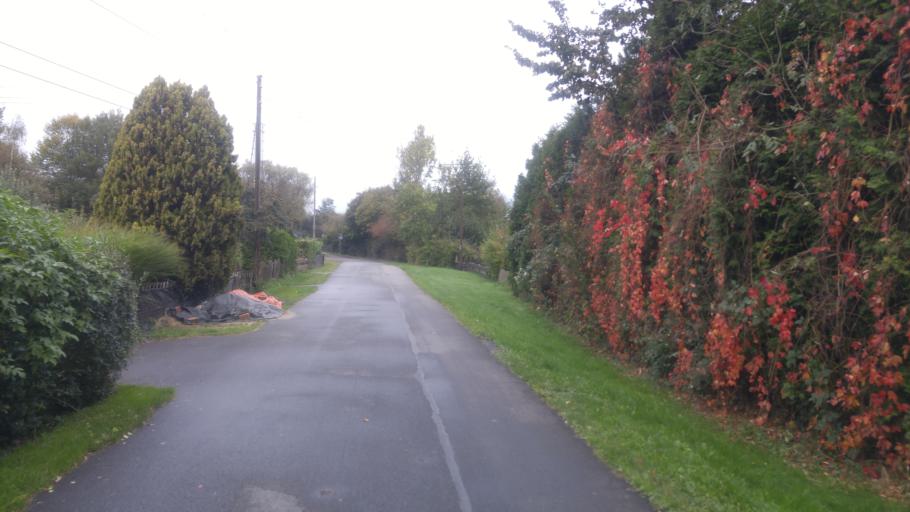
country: DE
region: Bremen
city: Bremen
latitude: 53.1108
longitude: 8.8201
